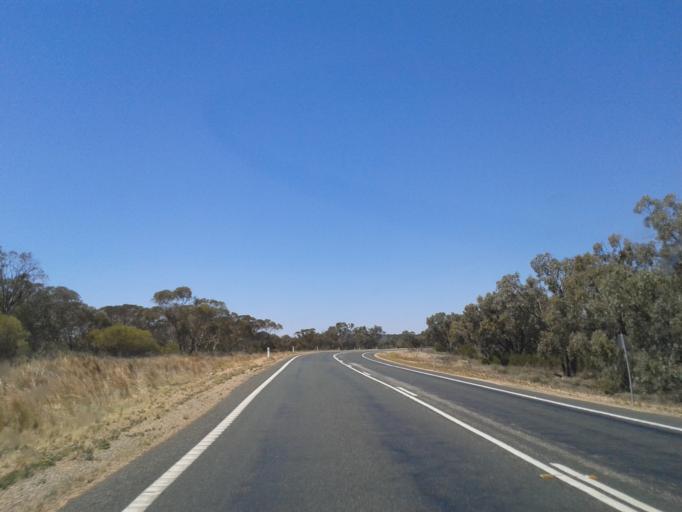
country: AU
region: New South Wales
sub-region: Wentworth
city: Gol Gol
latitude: -34.2928
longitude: 142.3196
